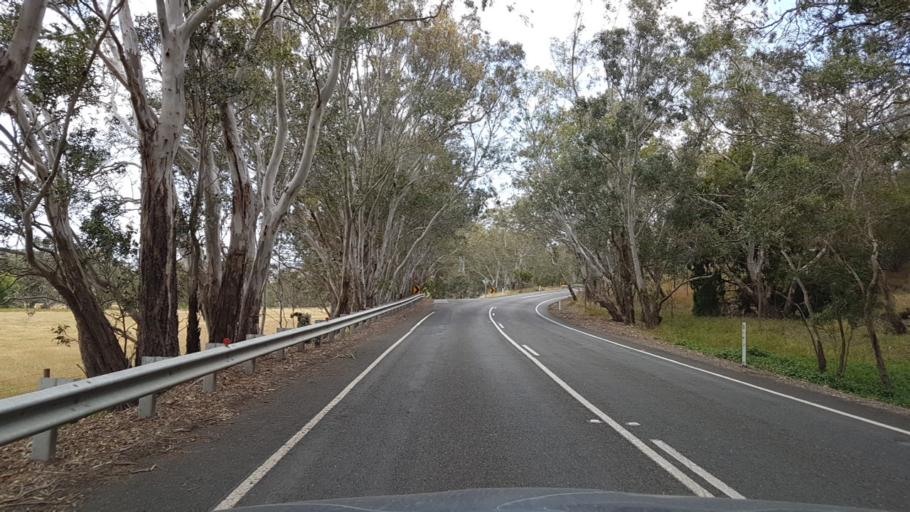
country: AU
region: South Australia
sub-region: Victor Harbor
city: Victor Harbor
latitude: -35.4808
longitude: 138.6102
